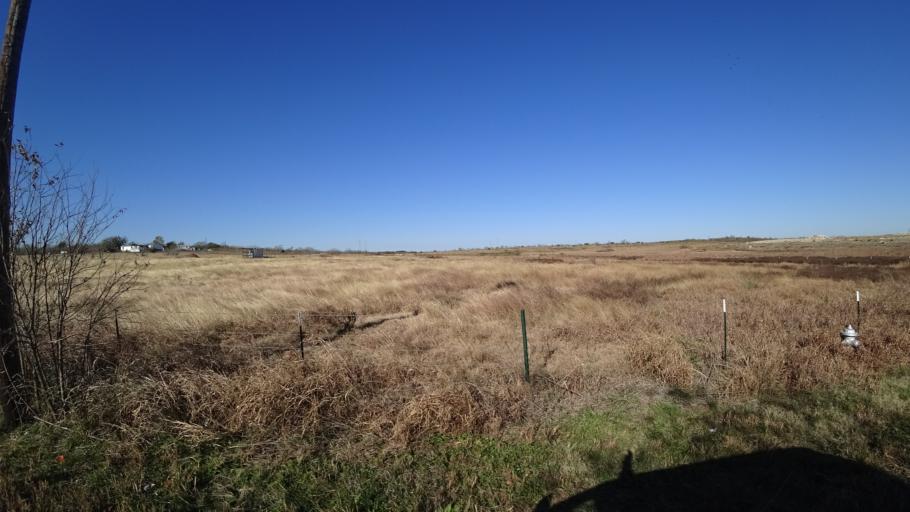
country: US
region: Texas
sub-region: Travis County
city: Onion Creek
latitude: 30.1159
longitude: -97.6714
